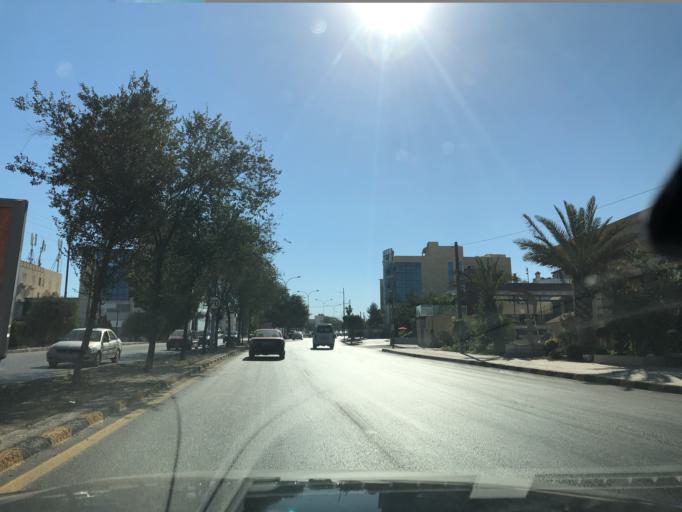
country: JO
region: Amman
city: Al Jubayhah
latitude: 31.9734
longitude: 35.8717
